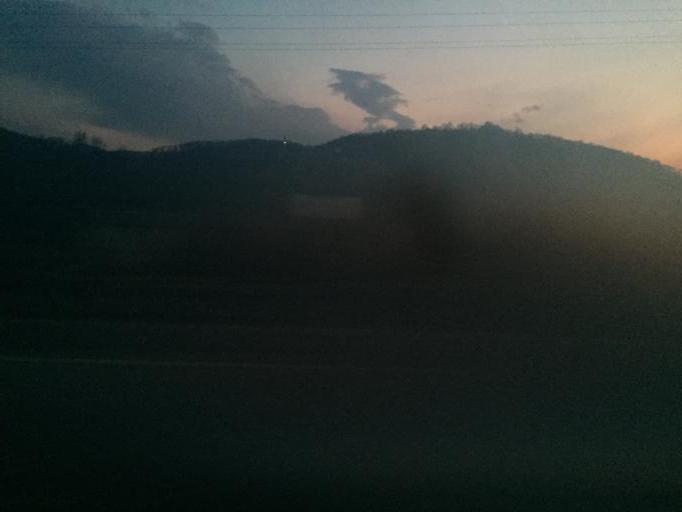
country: TR
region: Samsun
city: Kavak
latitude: 41.1370
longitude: 36.1251
